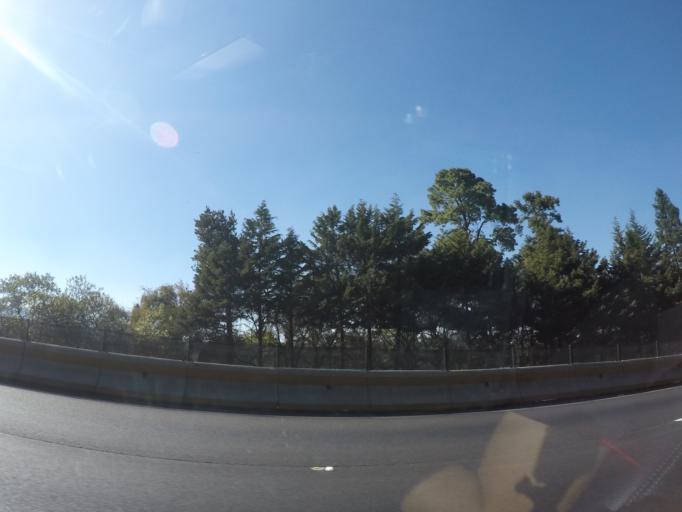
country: MX
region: Mexico City
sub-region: Cuajimalpa de Morelos
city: San Lorenzo Acopilco
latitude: 19.3251
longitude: -99.3181
